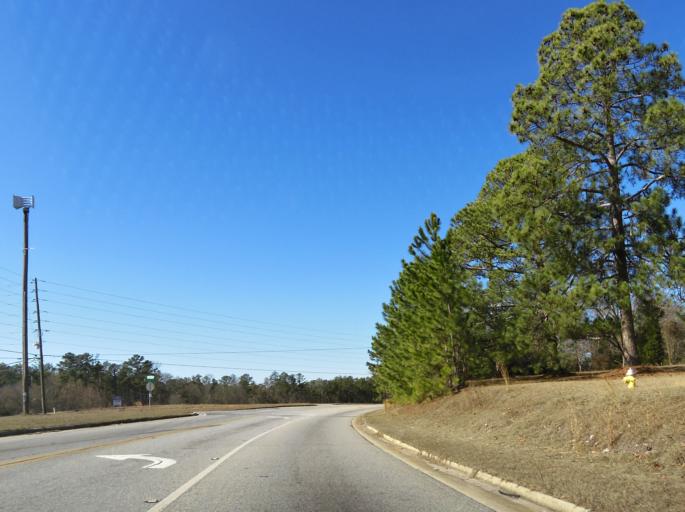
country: US
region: Georgia
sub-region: Bibb County
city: West Point
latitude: 32.7440
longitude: -83.7263
